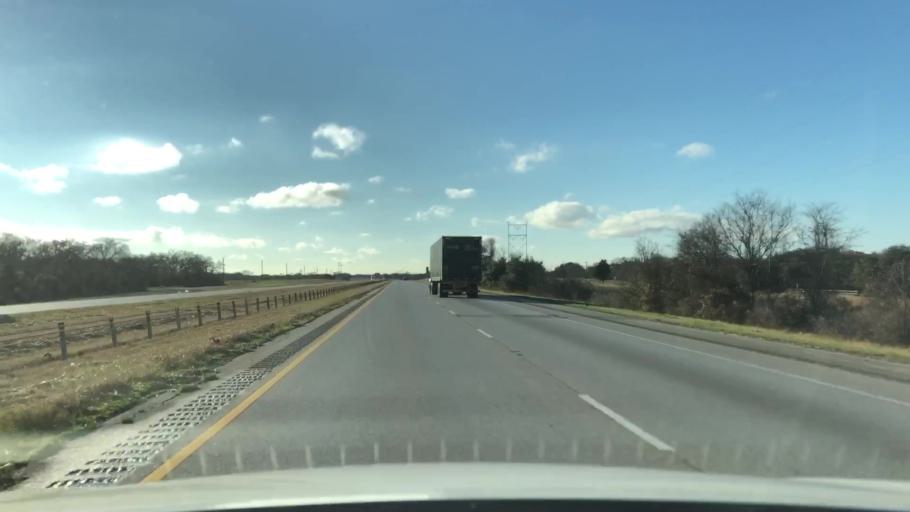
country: US
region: Texas
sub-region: Colorado County
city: Weimar
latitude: 29.6894
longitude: -96.6871
